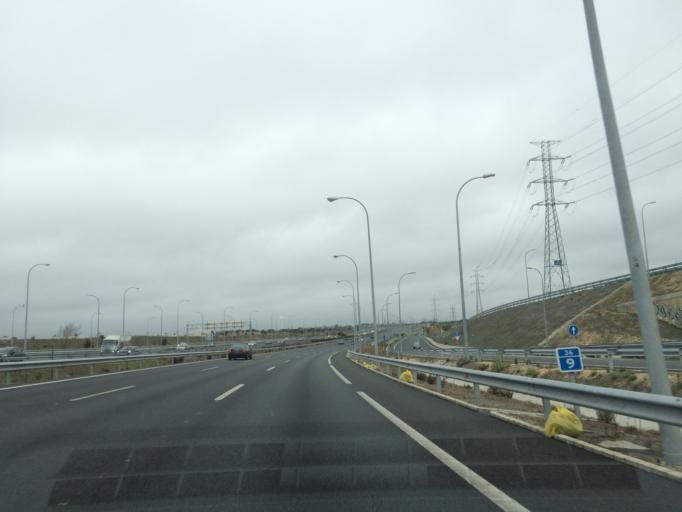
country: ES
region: Madrid
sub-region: Provincia de Madrid
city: Pozuelo de Alarcon
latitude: 40.3992
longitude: -3.8326
